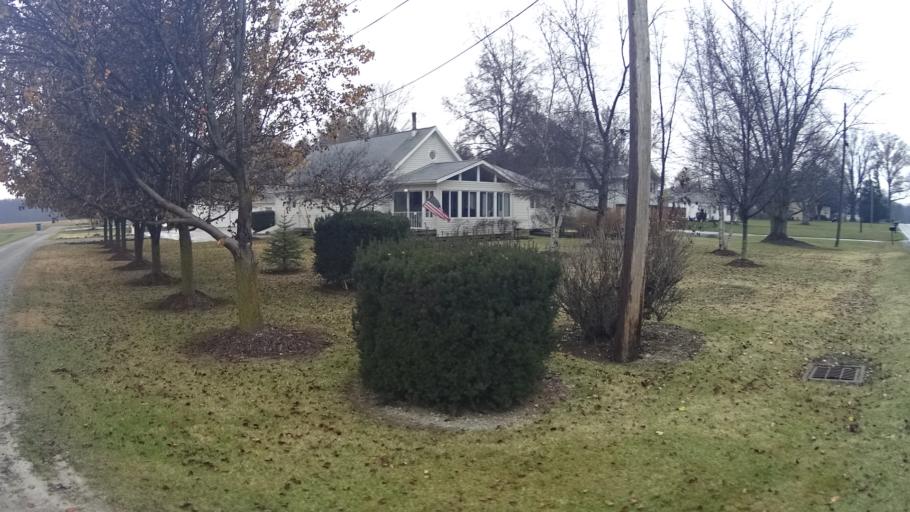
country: US
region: Ohio
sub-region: Lorain County
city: Grafton
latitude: 41.3152
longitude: -82.0906
